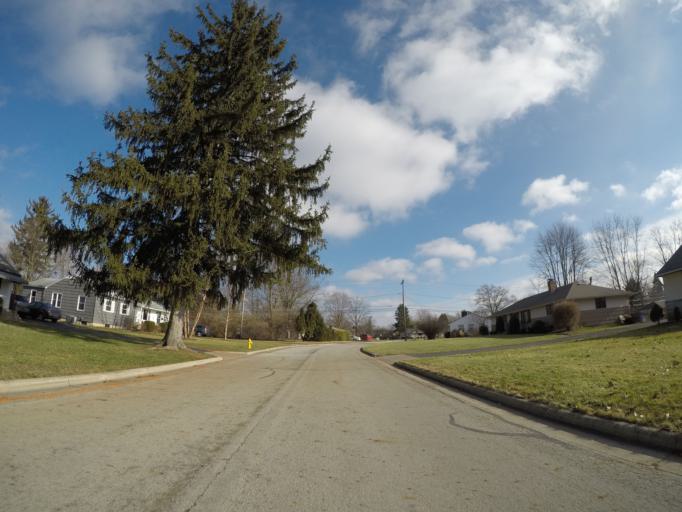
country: US
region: Ohio
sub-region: Franklin County
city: Upper Arlington
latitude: 40.0270
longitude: -83.0705
